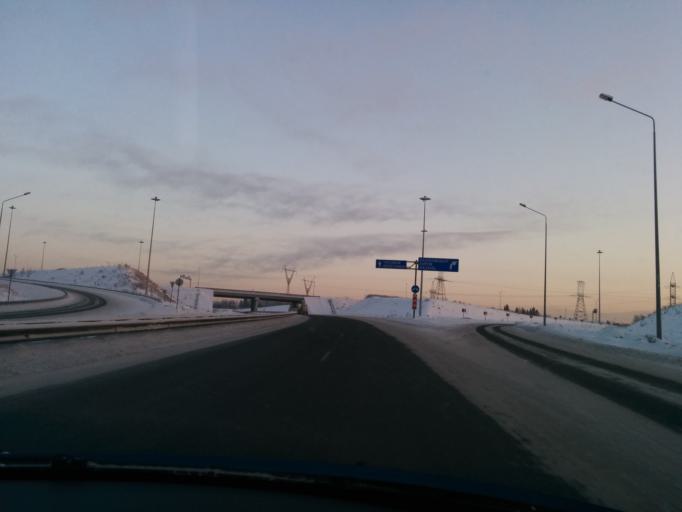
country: RU
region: Perm
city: Ferma
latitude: 57.9996
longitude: 56.3813
